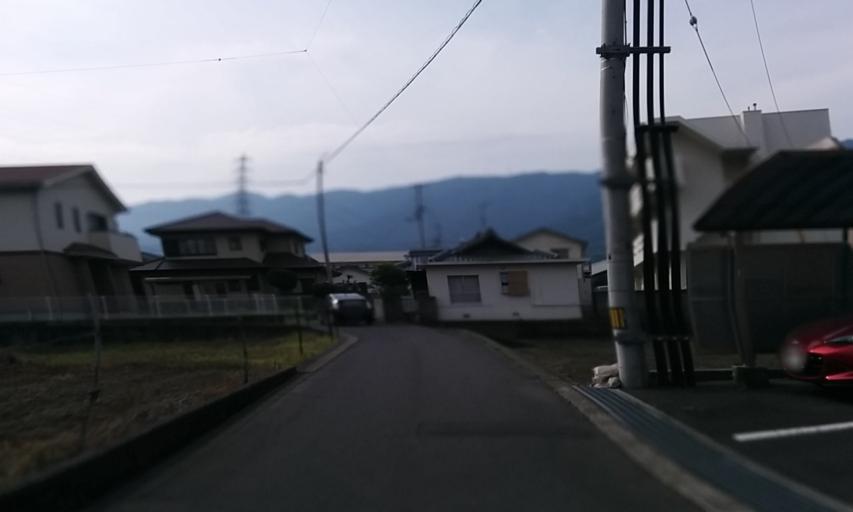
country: JP
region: Ehime
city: Kawanoecho
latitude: 33.9842
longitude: 133.5538
